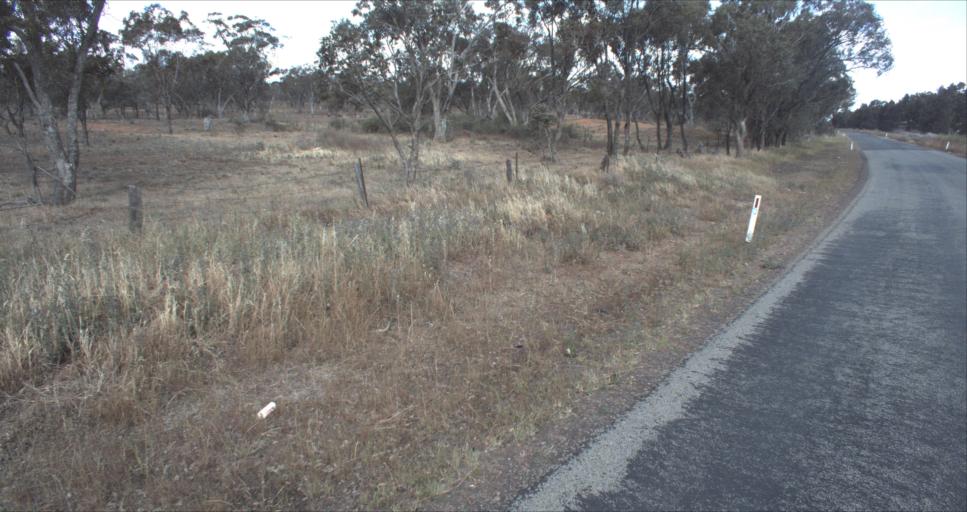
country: AU
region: New South Wales
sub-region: Griffith
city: Griffith
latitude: -34.4088
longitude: 146.2162
